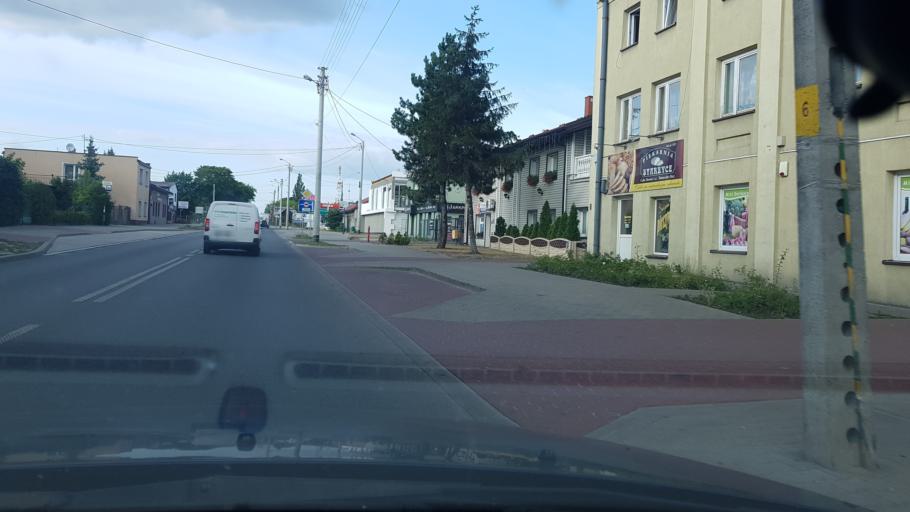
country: PL
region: Lodz Voivodeship
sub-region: Powiat tomaszowski
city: Tomaszow Mazowiecki
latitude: 51.5521
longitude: 20.0171
